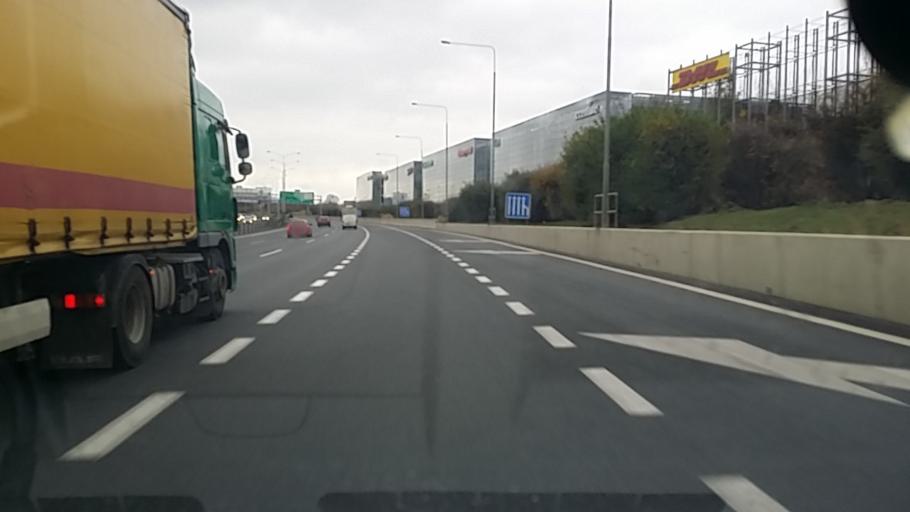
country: CZ
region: Central Bohemia
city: Vestec
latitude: 50.0292
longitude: 14.4947
